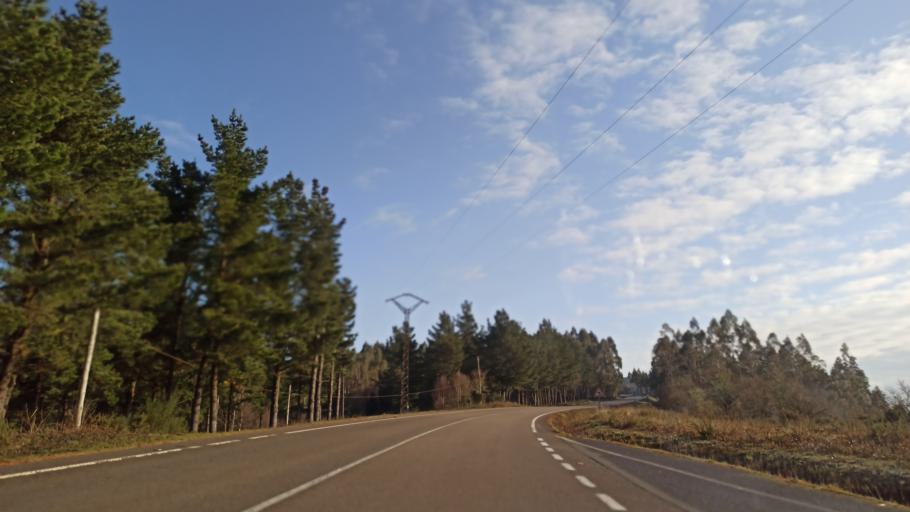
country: ES
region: Galicia
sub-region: Provincia da Coruna
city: As Pontes de Garcia Rodriguez
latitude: 43.5014
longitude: -7.8277
